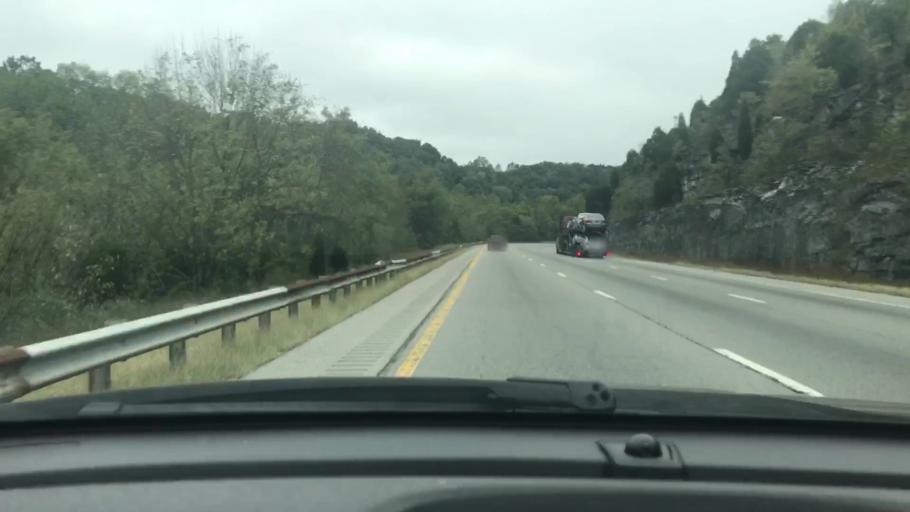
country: US
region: Tennessee
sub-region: Sumner County
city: Millersville
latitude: 36.4078
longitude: -86.7203
